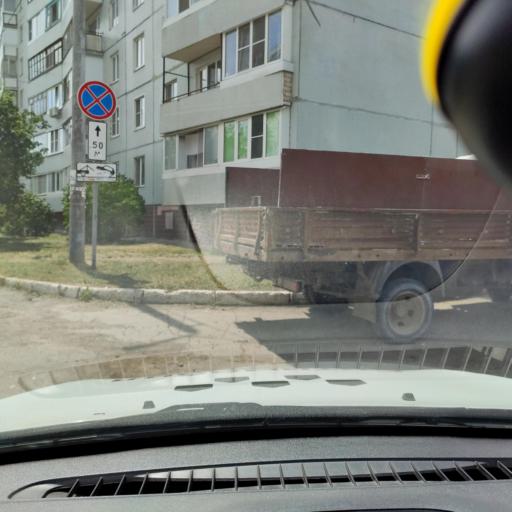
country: RU
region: Samara
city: Zhigulevsk
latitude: 53.4035
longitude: 49.5321
